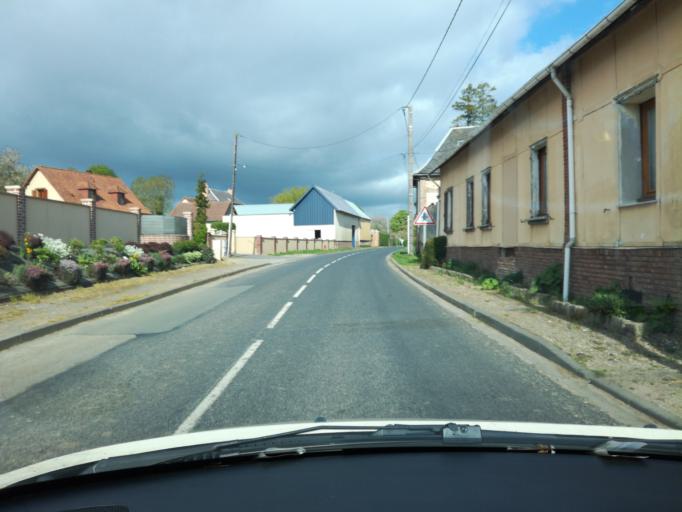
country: FR
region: Picardie
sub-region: Departement de la Somme
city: Beaucamps-le-Vieux
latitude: 49.8706
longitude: 1.8298
